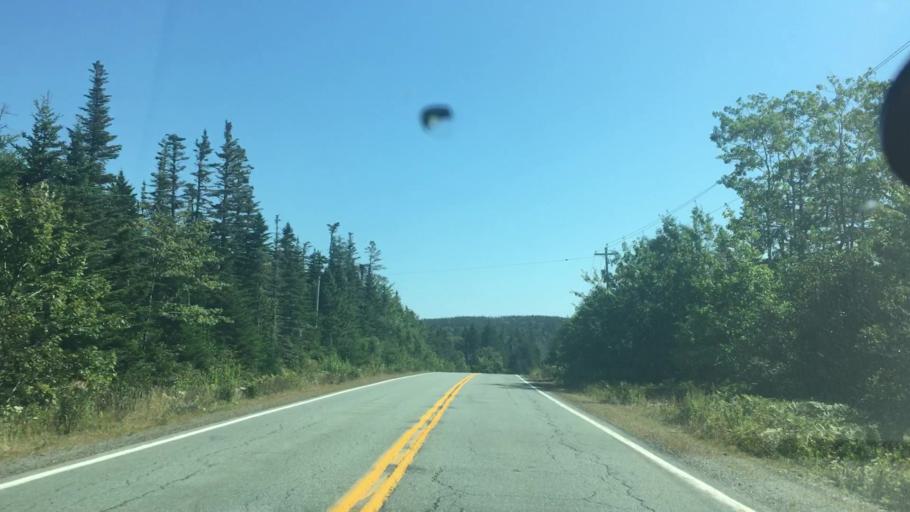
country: CA
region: Nova Scotia
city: Antigonish
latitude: 45.0133
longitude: -62.1006
